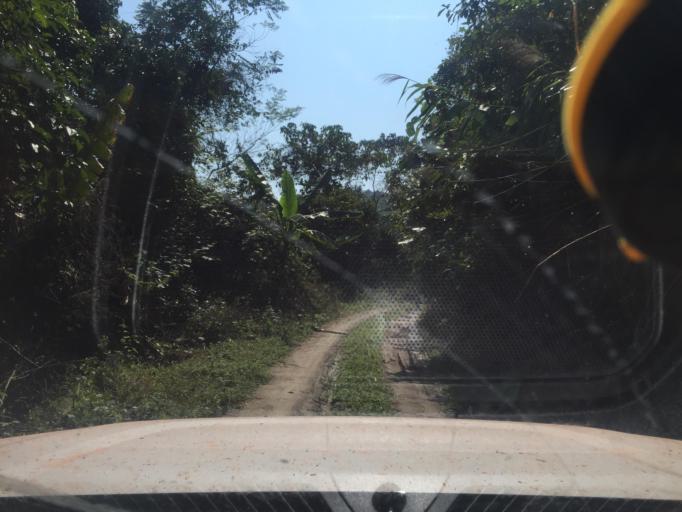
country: LA
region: Phongsali
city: Phongsali
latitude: 21.6887
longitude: 102.4092
